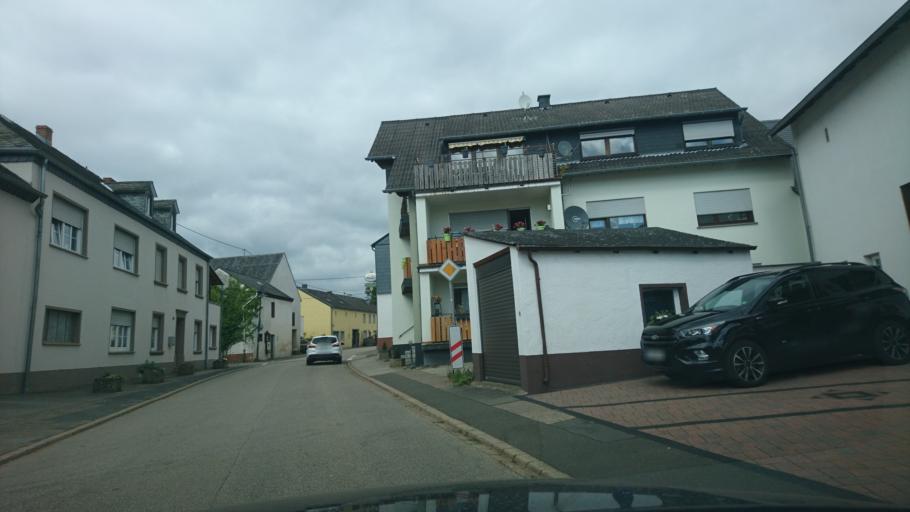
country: DE
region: Rheinland-Pfalz
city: Wiltingen
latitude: 49.6582
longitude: 6.5902
